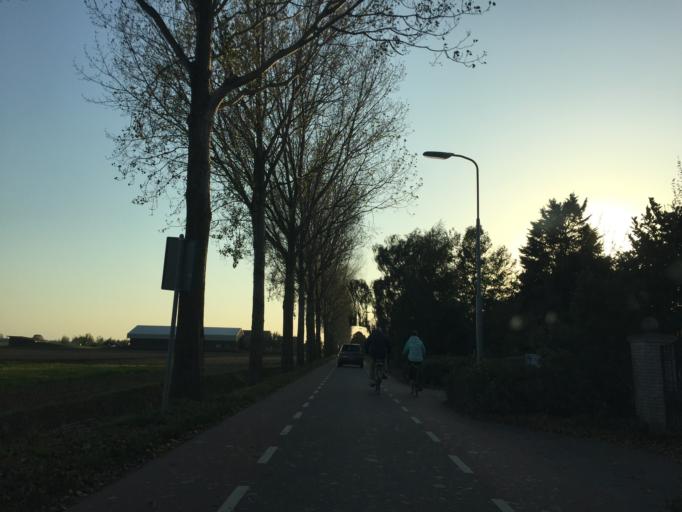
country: NL
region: South Holland
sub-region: Gemeente Kaag en Braassem
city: Oude Wetering
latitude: 52.2284
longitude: 4.6221
